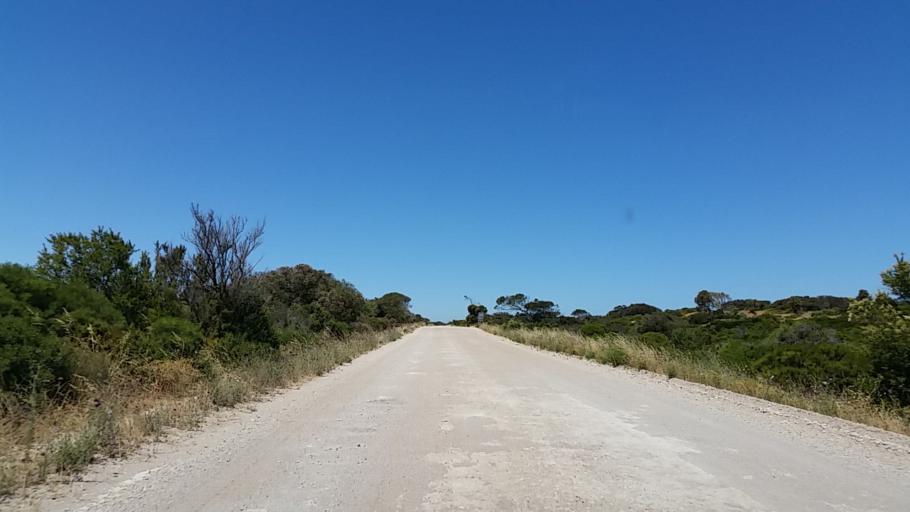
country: AU
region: South Australia
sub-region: Yorke Peninsula
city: Honiton
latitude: -35.1177
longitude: 137.3647
